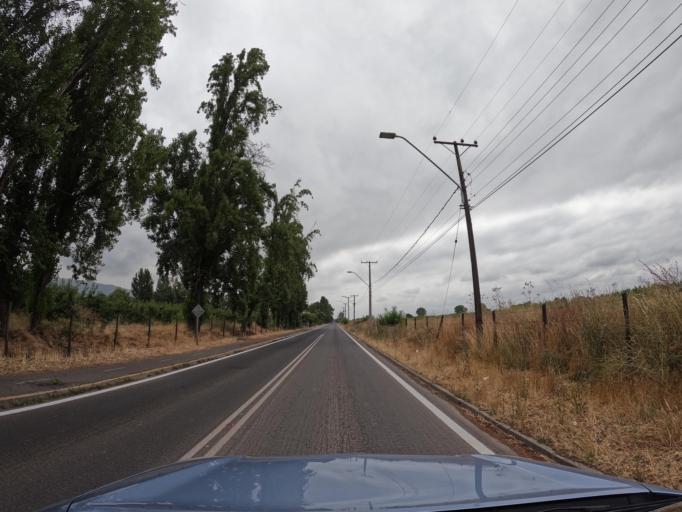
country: CL
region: O'Higgins
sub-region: Provincia de Colchagua
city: Chimbarongo
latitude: -34.7340
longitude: -71.0627
